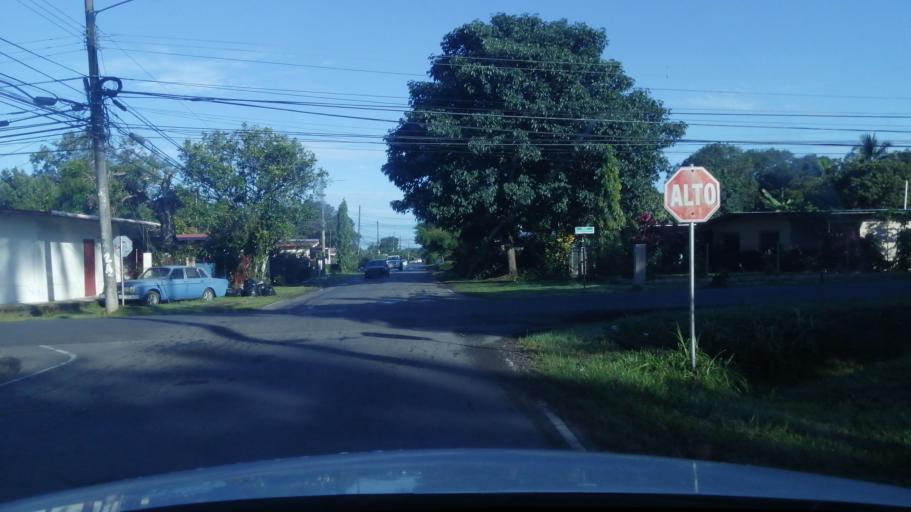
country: PA
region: Chiriqui
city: David
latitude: 8.4231
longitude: -82.4347
